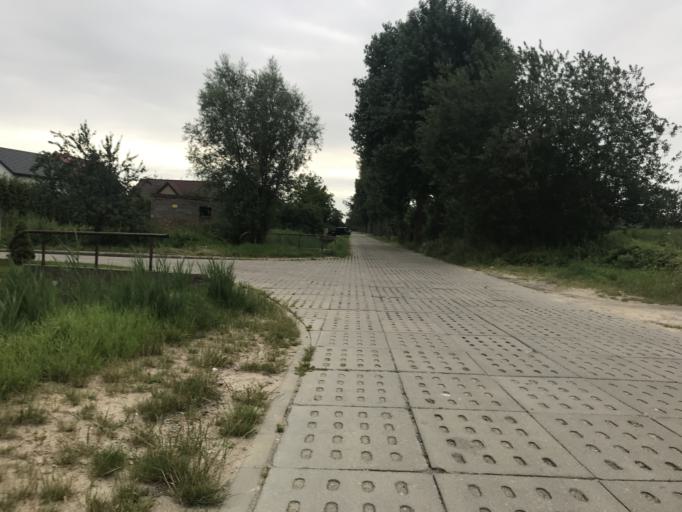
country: PL
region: Pomeranian Voivodeship
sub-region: Gdansk
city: Gdansk
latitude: 54.3442
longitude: 18.6744
